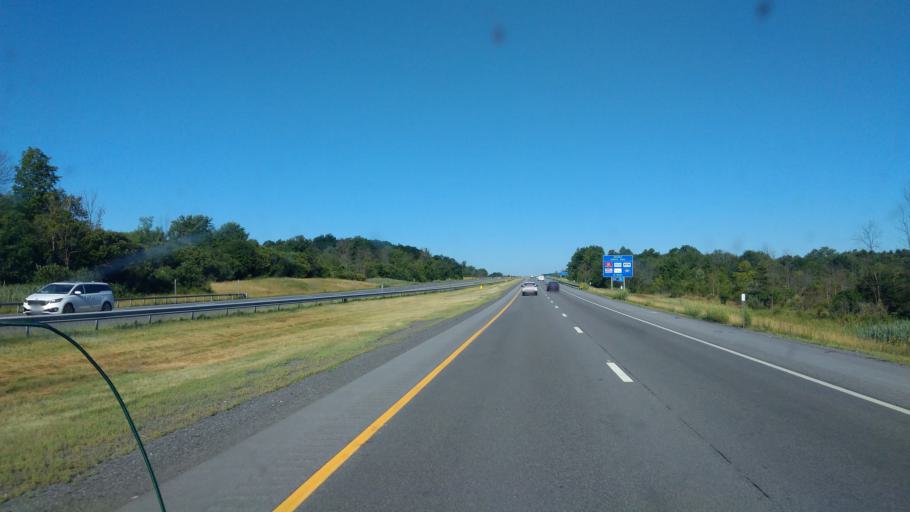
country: US
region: New York
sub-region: Livingston County
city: Caledonia
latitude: 43.0300
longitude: -77.8649
